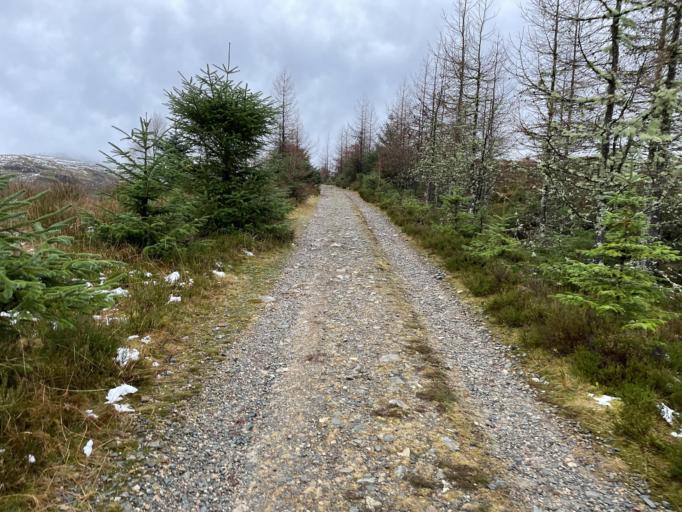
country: GB
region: Scotland
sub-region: Highland
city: Fort William
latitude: 56.8109
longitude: -5.0947
